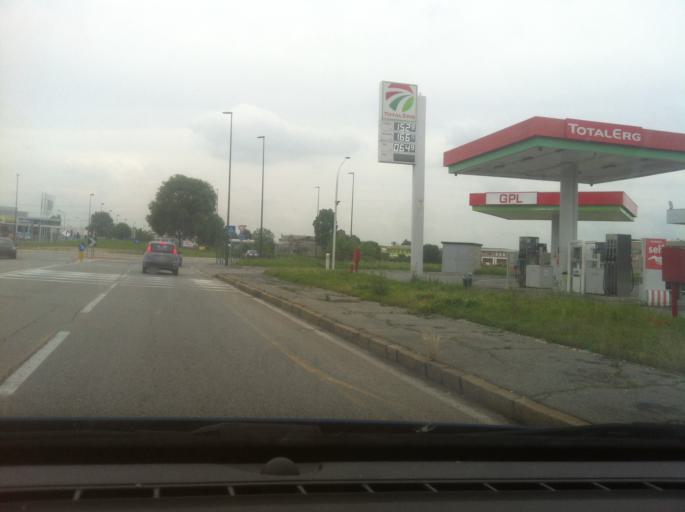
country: IT
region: Piedmont
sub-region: Provincia di Torino
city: San Mauro Torinese
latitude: 45.1087
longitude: 7.7285
